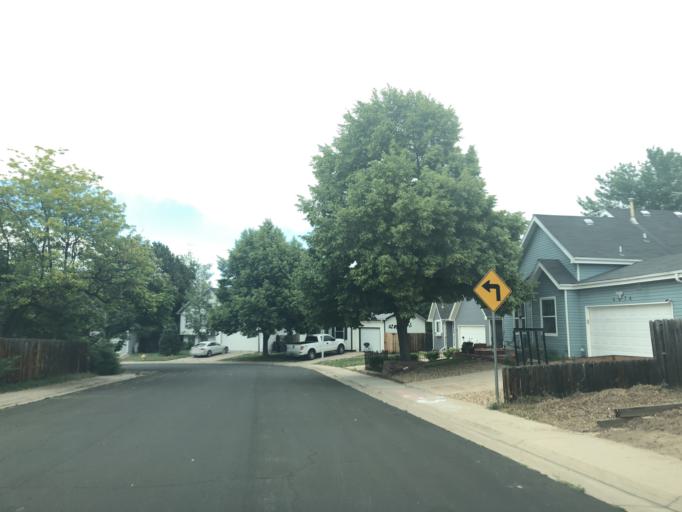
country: US
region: Colorado
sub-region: Arapahoe County
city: Dove Valley
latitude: 39.6289
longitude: -104.7807
